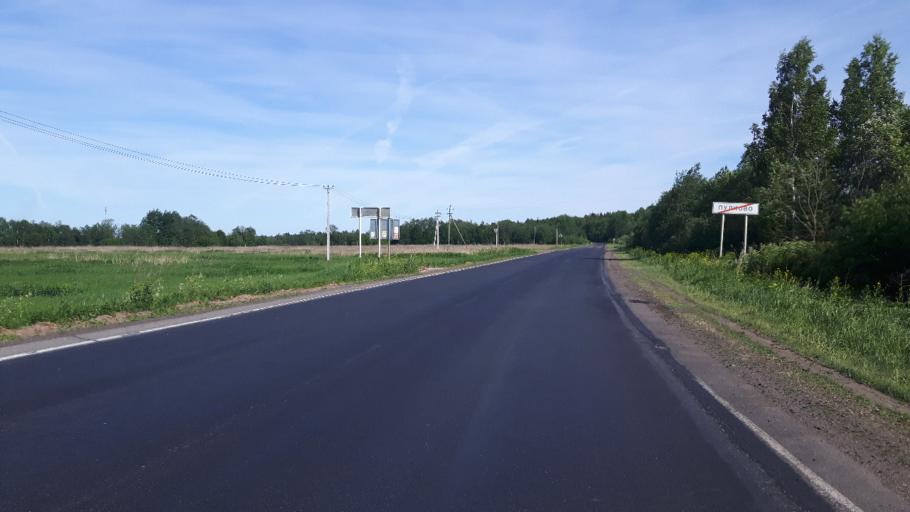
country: RU
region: Leningrad
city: Ivangorod
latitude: 59.4188
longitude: 28.3595
